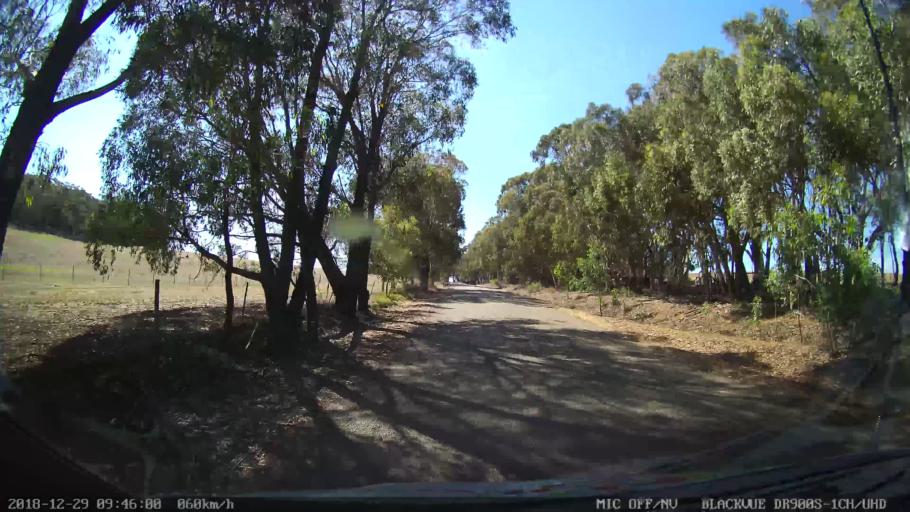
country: AU
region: New South Wales
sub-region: Upper Lachlan Shire
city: Crookwell
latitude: -34.6994
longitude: 149.4402
